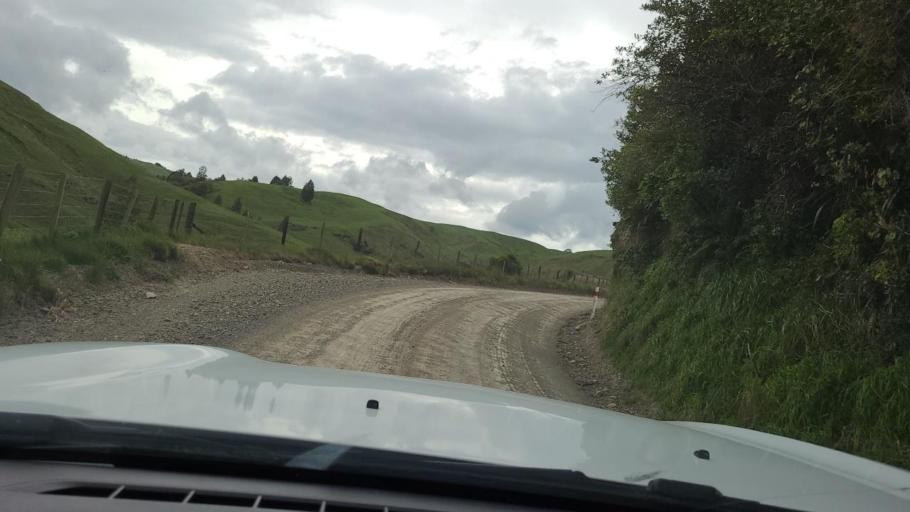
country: NZ
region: Hawke's Bay
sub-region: Napier City
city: Napier
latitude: -39.2702
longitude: 176.8383
